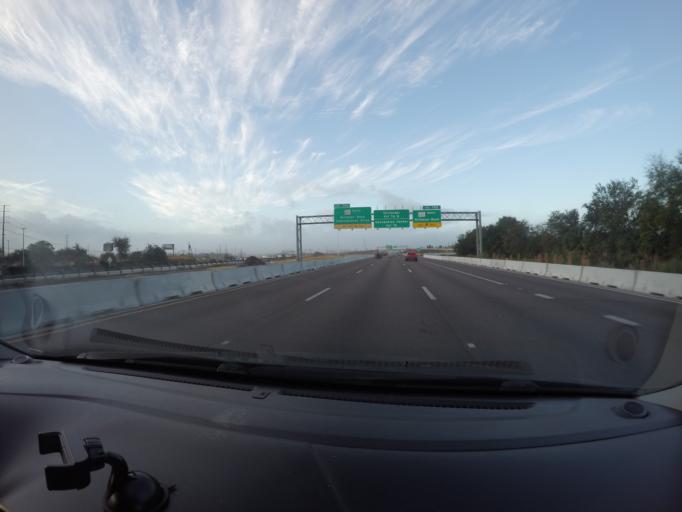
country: US
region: Florida
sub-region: Orange County
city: Tangelo Park
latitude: 28.4740
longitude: -81.4555
